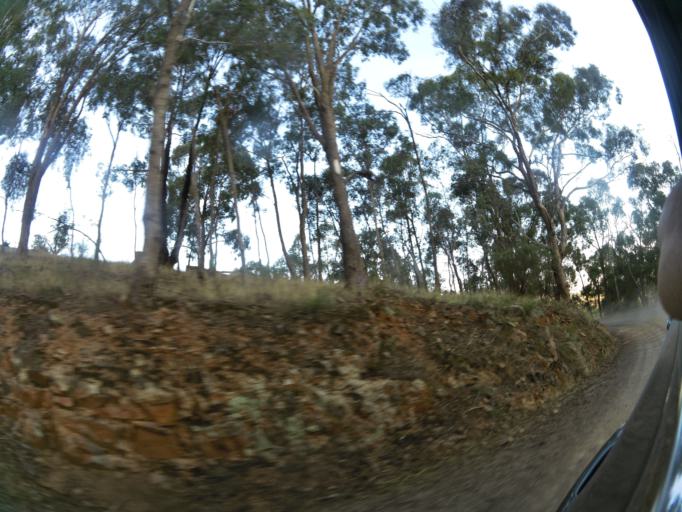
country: AU
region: Victoria
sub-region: Murrindindi
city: Alexandra
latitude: -37.1477
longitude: 145.5193
